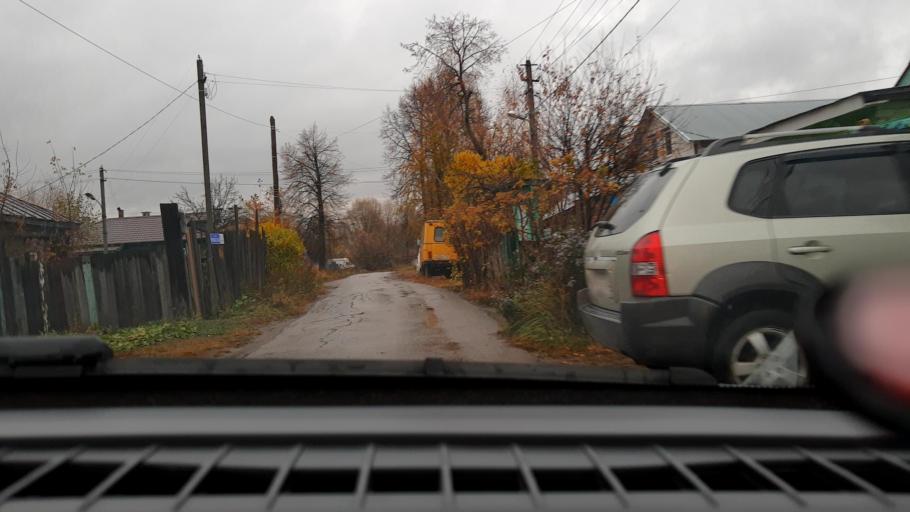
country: RU
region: Nizjnij Novgorod
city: Gorbatovka
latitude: 56.3029
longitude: 43.8433
